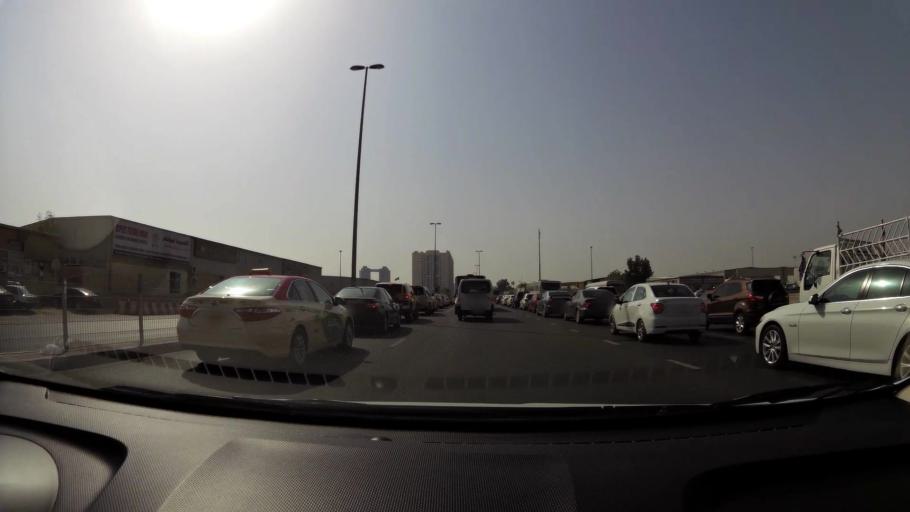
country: AE
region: Ash Shariqah
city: Sharjah
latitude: 25.2962
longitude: 55.3876
